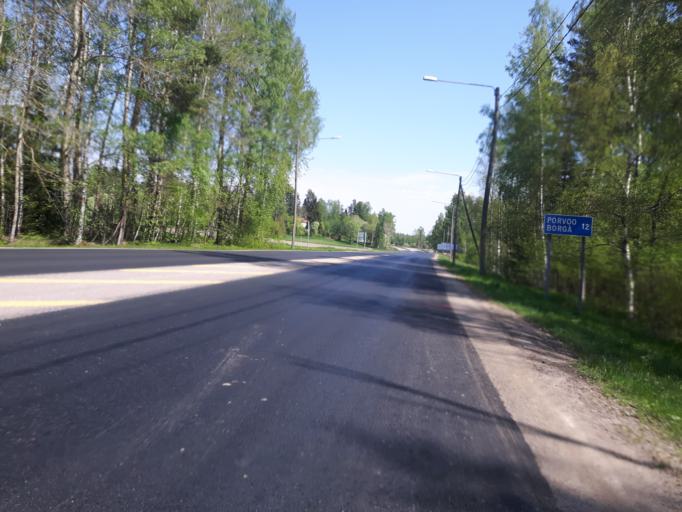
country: FI
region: Uusimaa
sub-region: Helsinki
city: Pornainen
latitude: 60.3414
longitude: 25.4744
